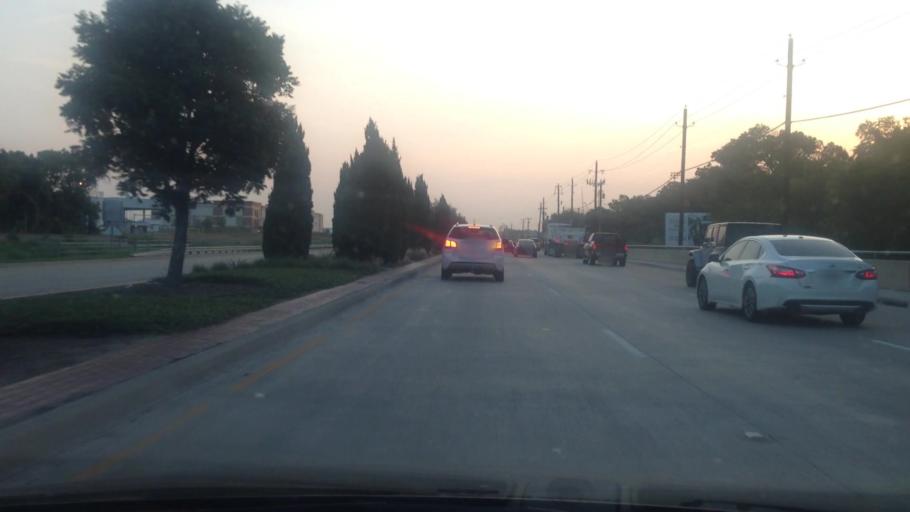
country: US
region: Texas
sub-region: Tarrant County
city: Southlake
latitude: 32.9166
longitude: -97.1233
